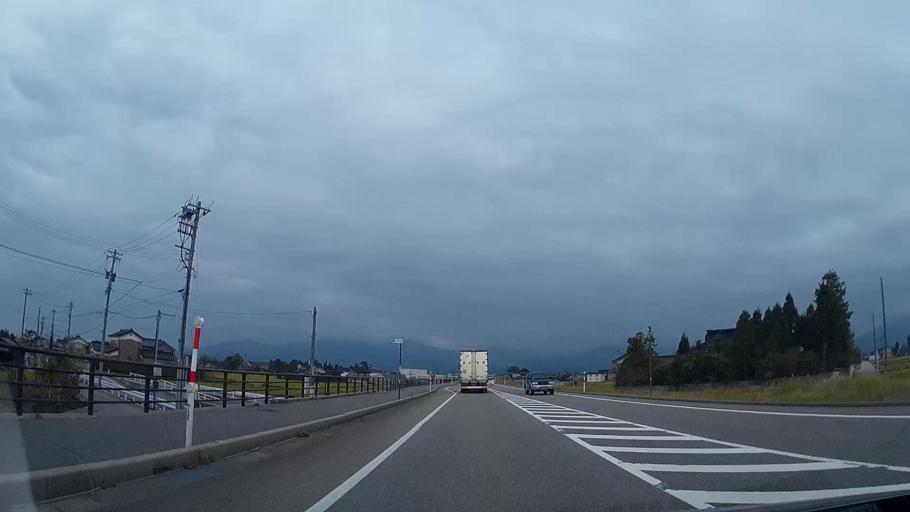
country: JP
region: Toyama
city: Nyuzen
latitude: 36.9278
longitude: 137.4821
